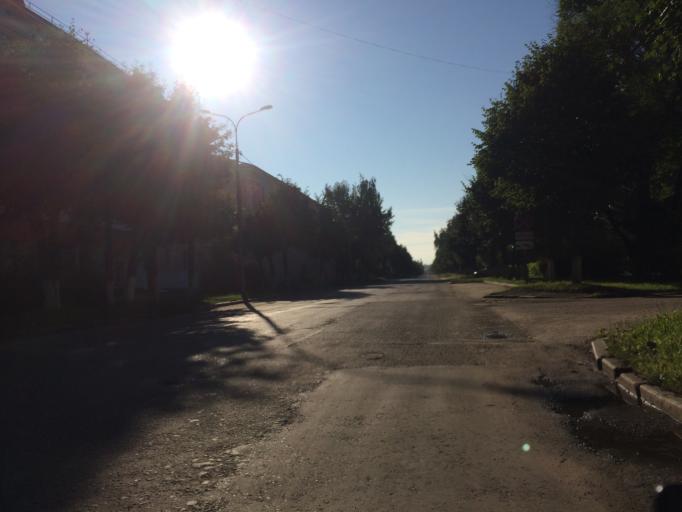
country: RU
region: Mariy-El
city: Yoshkar-Ola
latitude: 56.6411
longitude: 47.8817
